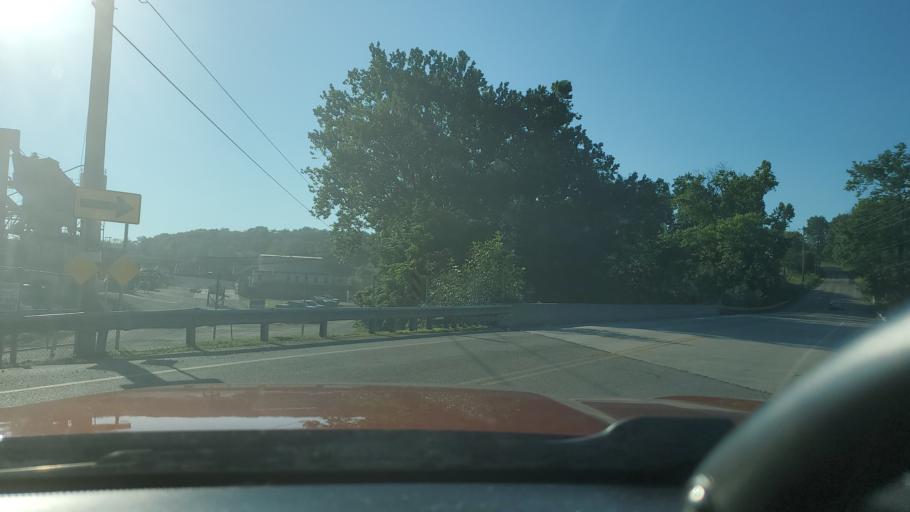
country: US
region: Pennsylvania
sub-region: Montgomery County
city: Woxall
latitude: 40.3228
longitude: -75.4730
